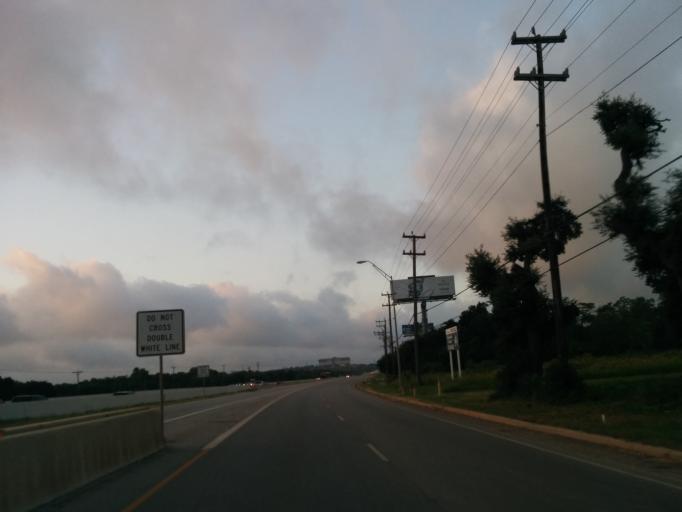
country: US
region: Texas
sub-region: Bexar County
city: Cross Mountain
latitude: 29.6363
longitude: -98.6148
